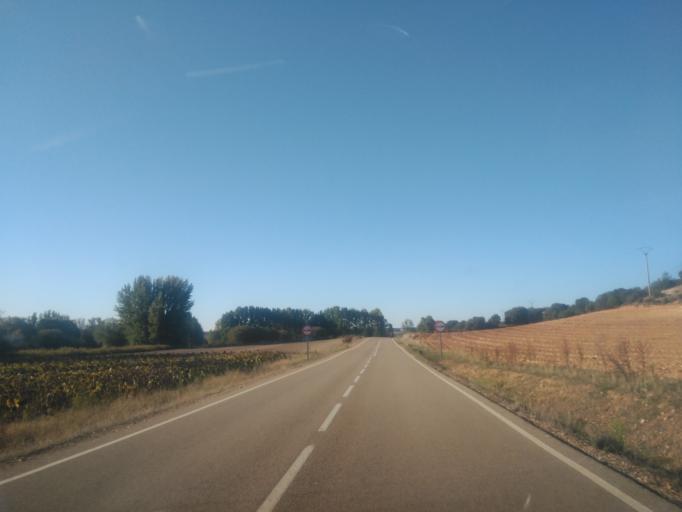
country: ES
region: Castille and Leon
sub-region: Provincia de Soria
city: Alcubilla de Avellaneda
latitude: 41.7391
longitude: -3.2935
